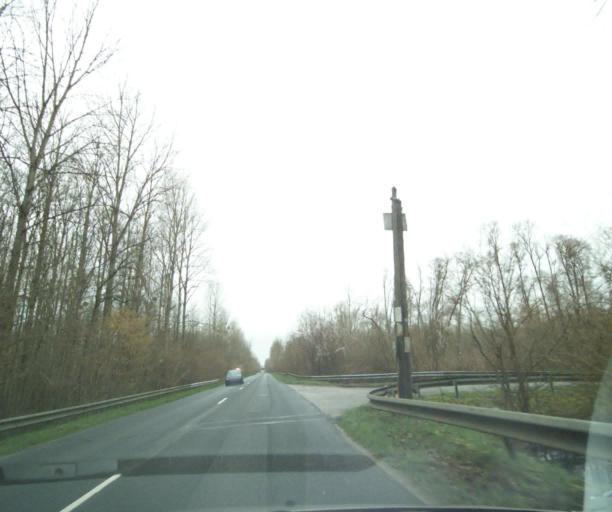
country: FR
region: Picardie
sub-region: Departement de l'Oise
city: Noyon
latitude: 49.5598
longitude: 3.0369
